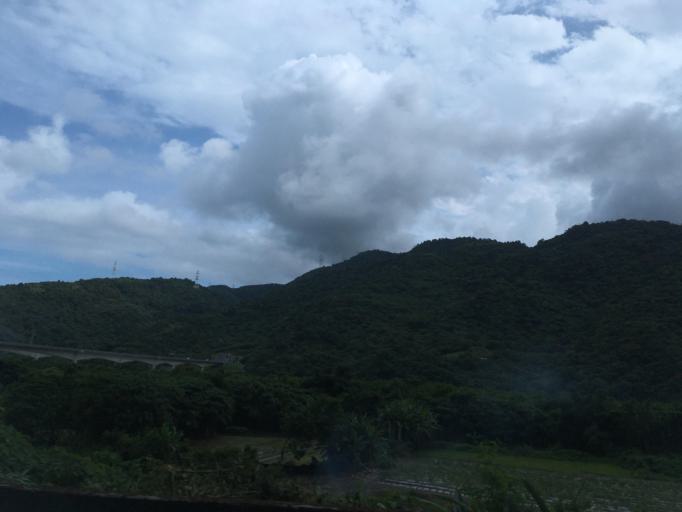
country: TW
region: Taiwan
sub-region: Yilan
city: Yilan
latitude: 24.4434
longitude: 121.7707
